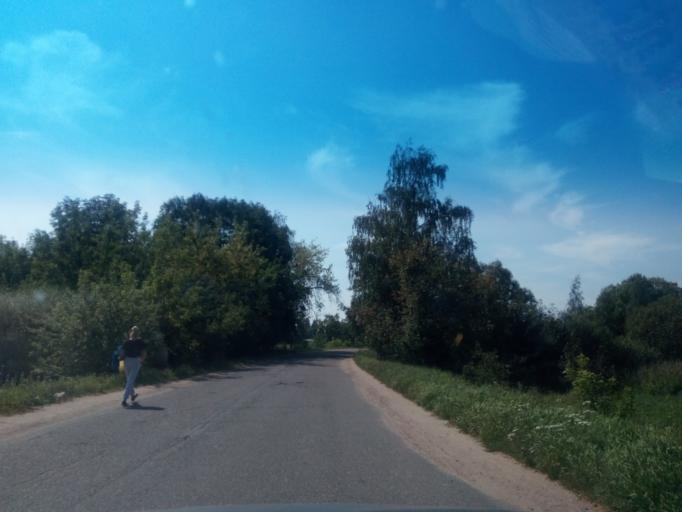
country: BY
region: Vitebsk
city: Vyerkhnyadzvinsk
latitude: 55.8363
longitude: 27.7386
